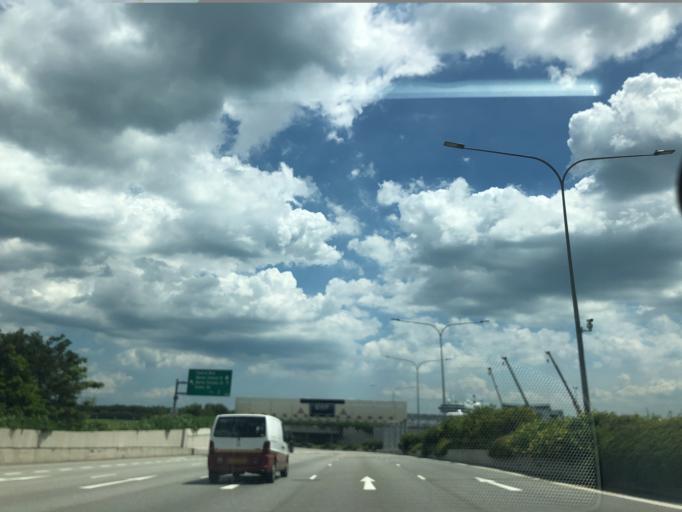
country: SG
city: Singapore
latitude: 1.2717
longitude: 103.8555
